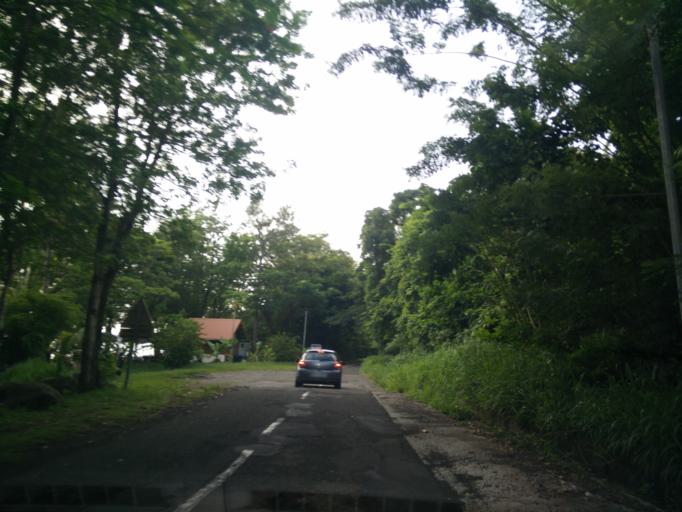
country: MQ
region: Martinique
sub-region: Martinique
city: Saint-Pierre
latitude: 14.8290
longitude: -61.2256
